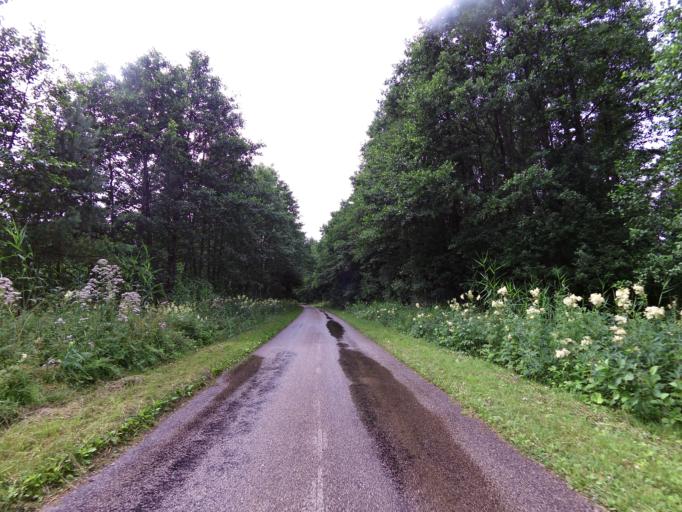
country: EE
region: Laeaene
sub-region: Vormsi vald
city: Hullo
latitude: 58.9973
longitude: 23.3407
